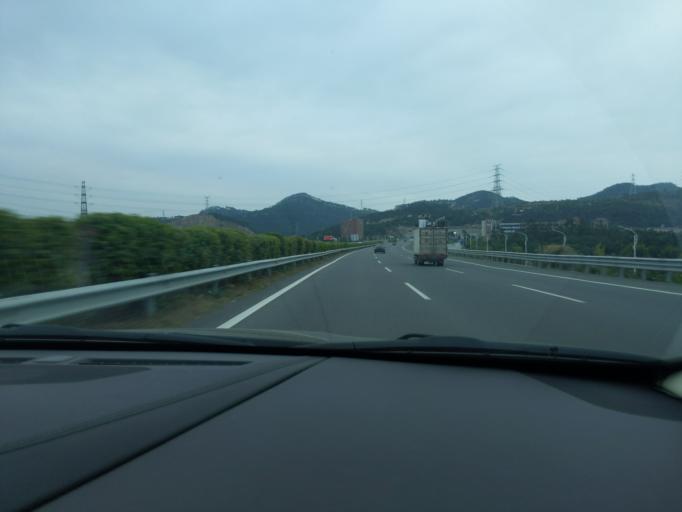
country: CN
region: Fujian
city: Cizao
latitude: 24.7812
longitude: 118.5048
